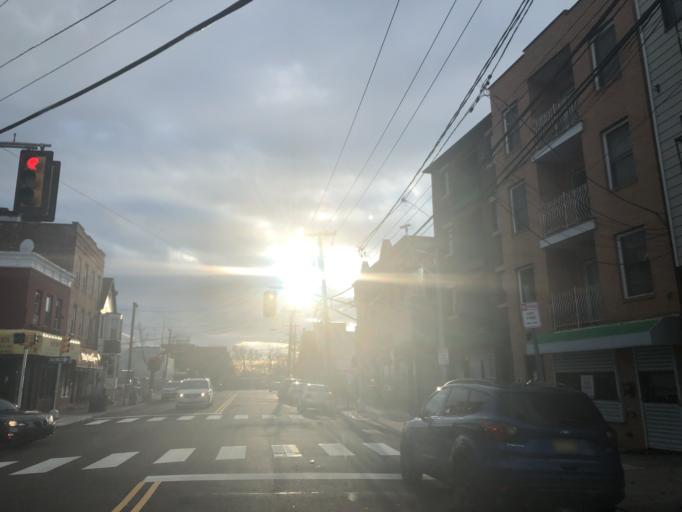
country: US
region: New Jersey
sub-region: Hudson County
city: Jersey City
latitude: 40.7143
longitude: -74.0885
